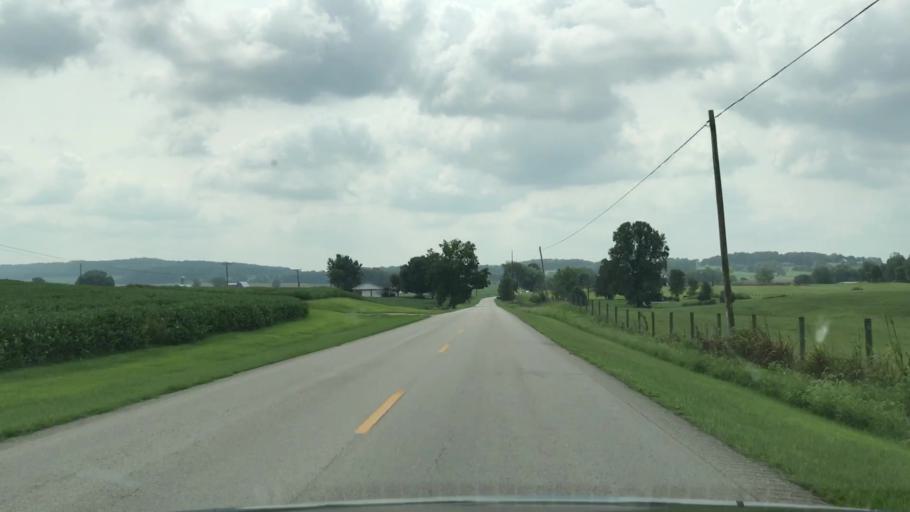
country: US
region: Kentucky
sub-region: Barren County
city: Cave City
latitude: 37.1025
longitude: -85.9779
